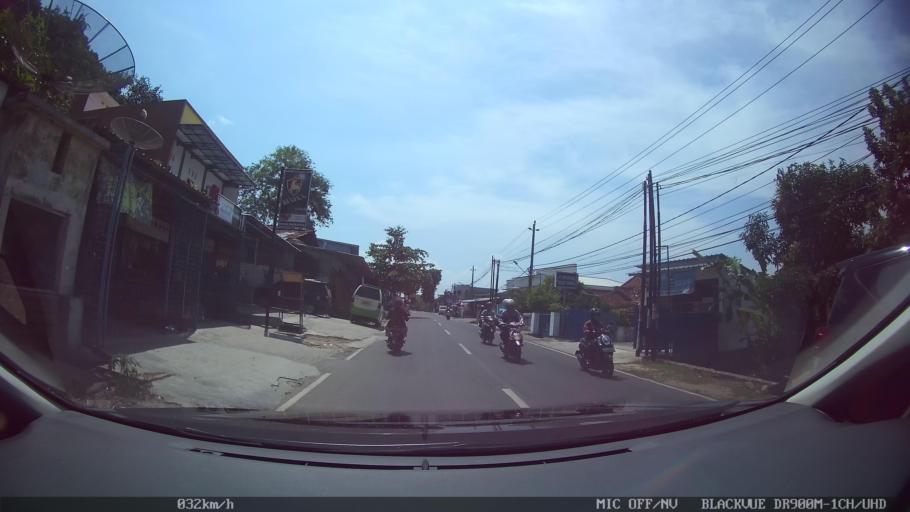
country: ID
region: Lampung
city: Kedaton
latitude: -5.3892
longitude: 105.2713
